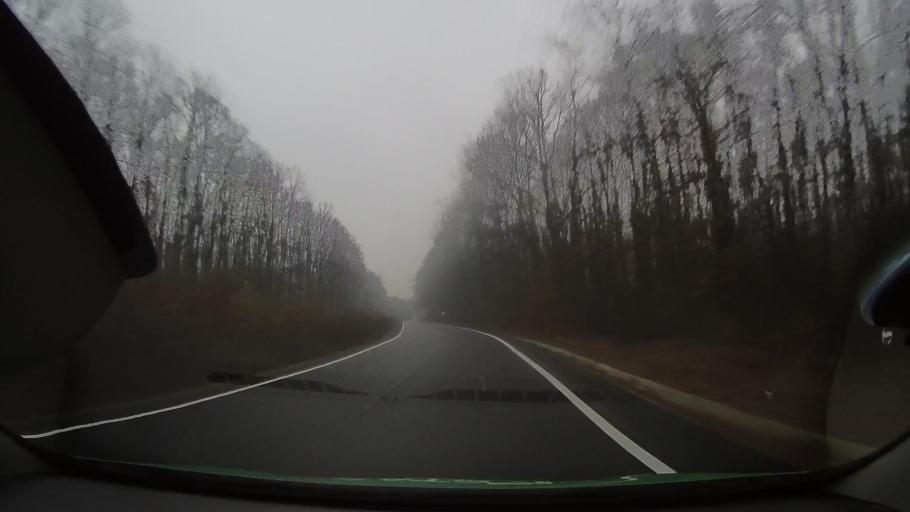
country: RO
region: Bihor
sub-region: Comuna Olcea
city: Olcea
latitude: 46.7022
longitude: 21.9637
